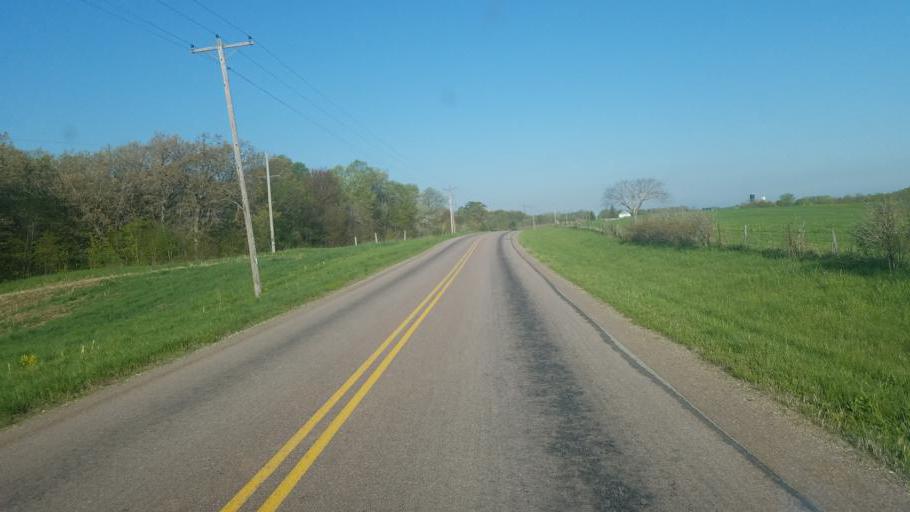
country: US
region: Wisconsin
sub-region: Vernon County
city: Hillsboro
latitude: 43.5949
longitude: -90.3989
